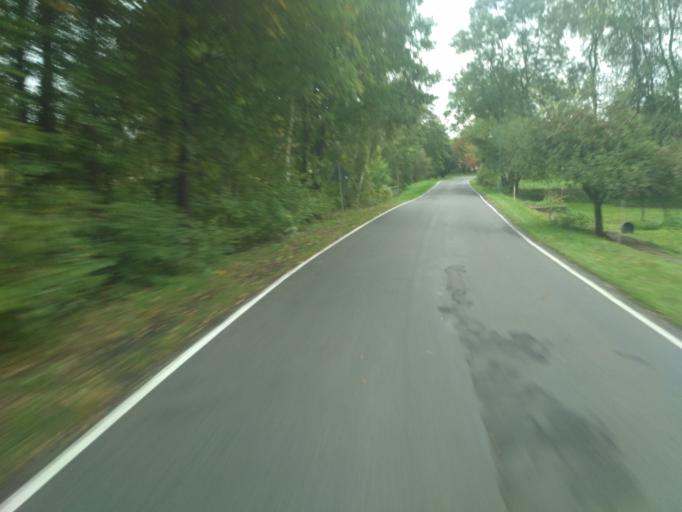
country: DE
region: Saxony
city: Wittichenau
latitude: 51.3659
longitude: 14.2630
